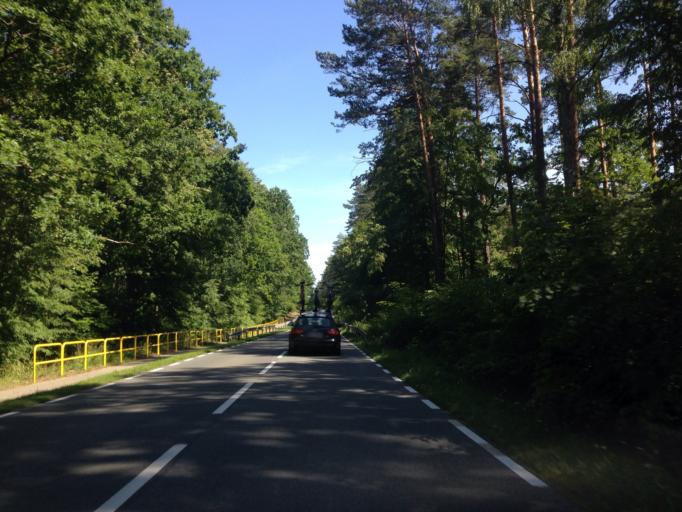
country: PL
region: Kujawsko-Pomorskie
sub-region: Powiat swiecki
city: Osie
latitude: 53.6090
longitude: 18.3059
